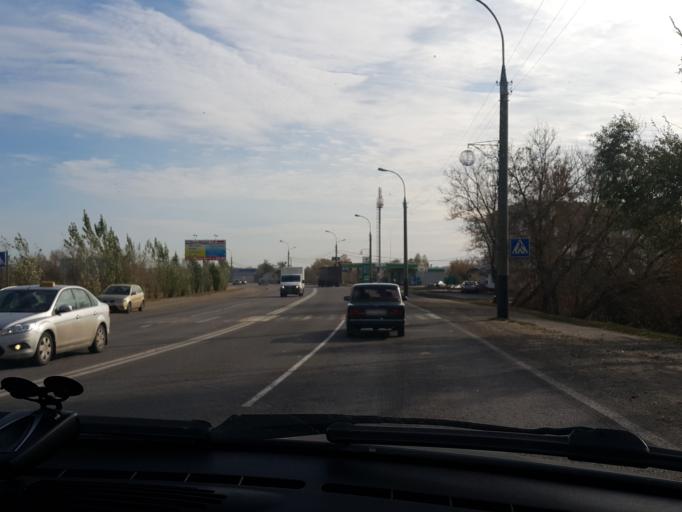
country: RU
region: Tambov
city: Tambov
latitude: 52.7252
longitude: 41.4665
